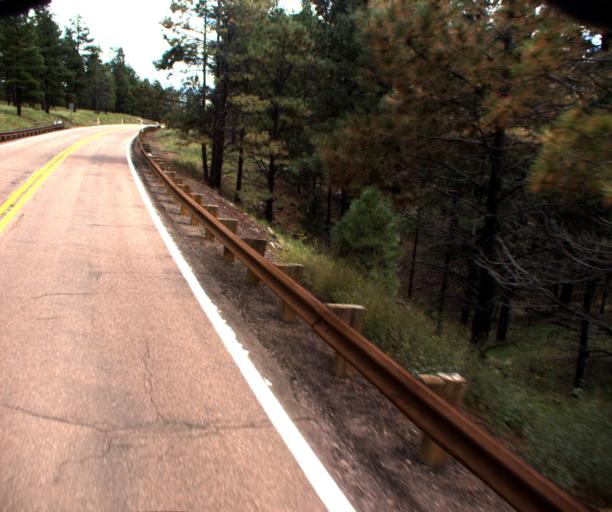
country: US
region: Arizona
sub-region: Apache County
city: Eagar
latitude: 34.0772
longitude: -109.4717
